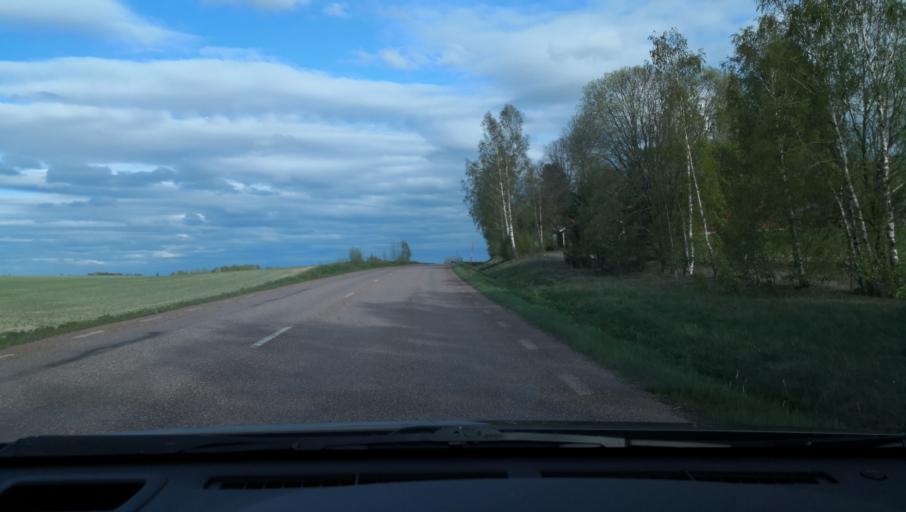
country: SE
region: Dalarna
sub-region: Hedemora Kommun
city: Hedemora
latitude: 60.2885
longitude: 15.9079
